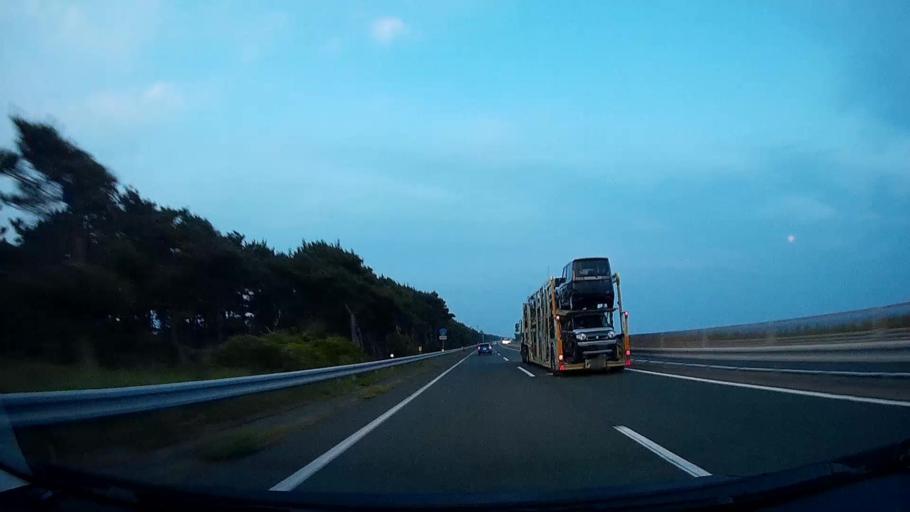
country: JP
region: Shizuoka
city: Kosai-shi
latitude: 34.6805
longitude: 137.5544
